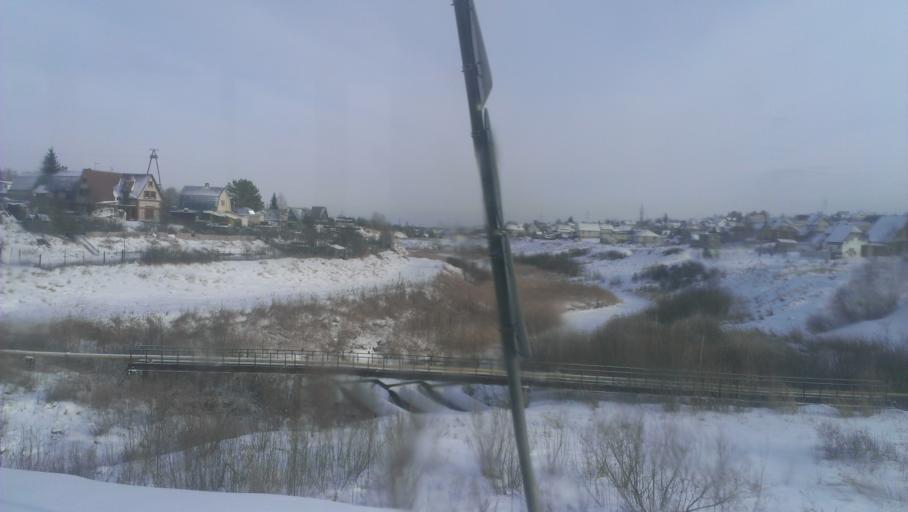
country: RU
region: Altai Krai
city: Gon'ba
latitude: 53.4153
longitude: 83.5505
